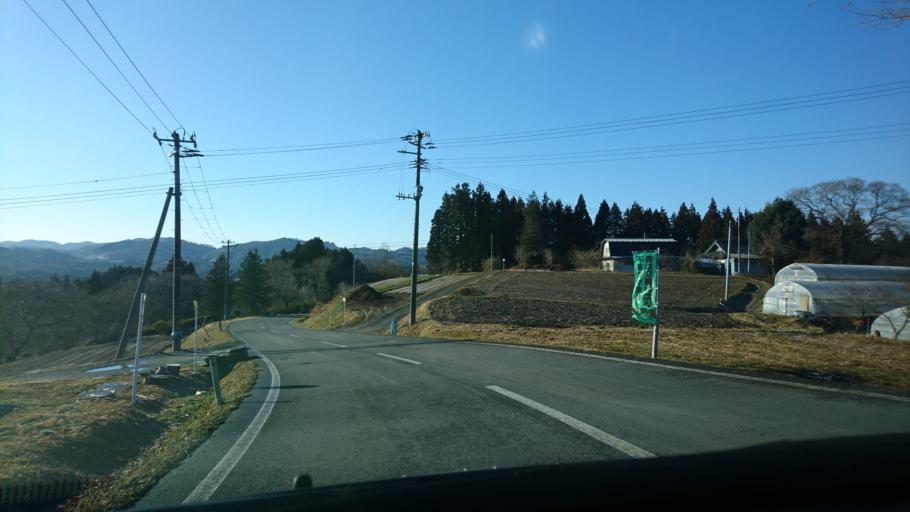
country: JP
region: Iwate
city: Ichinoseki
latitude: 38.8580
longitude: 141.2974
